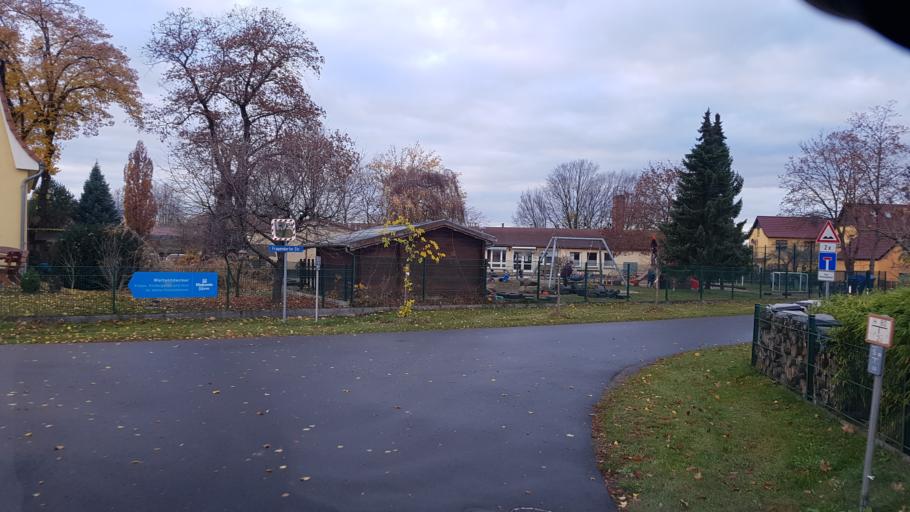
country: DE
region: Brandenburg
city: Kroppen
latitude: 51.3848
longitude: 13.7931
